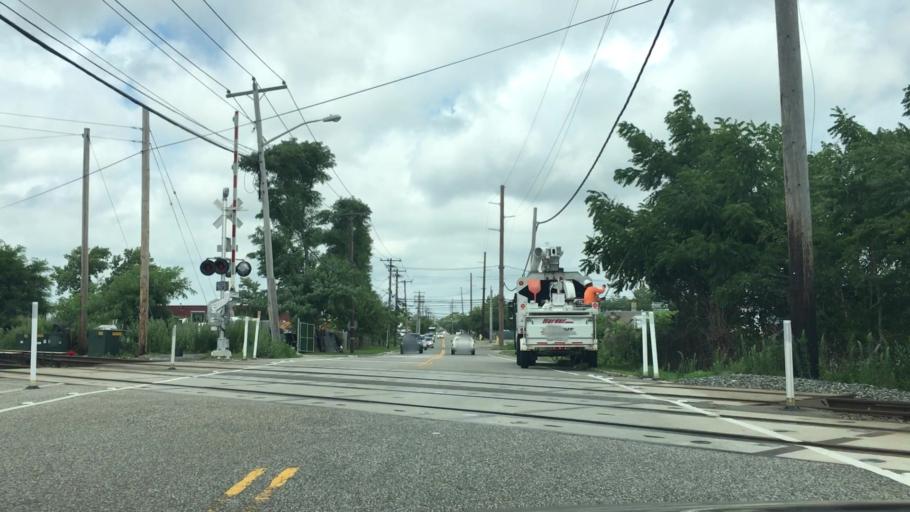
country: US
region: New York
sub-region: Nassau County
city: Hicksville
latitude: 40.7576
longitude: -73.5060
